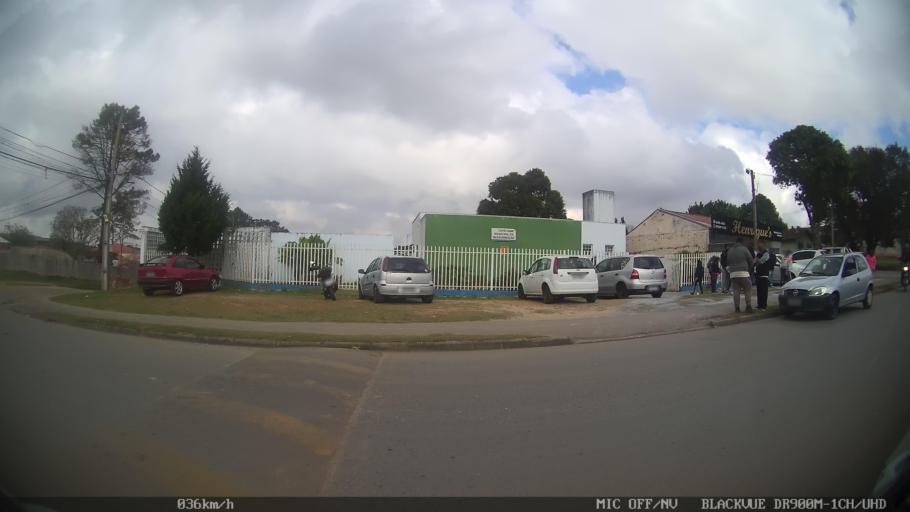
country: BR
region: Parana
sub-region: Colombo
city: Colombo
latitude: -25.3460
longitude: -49.2469
